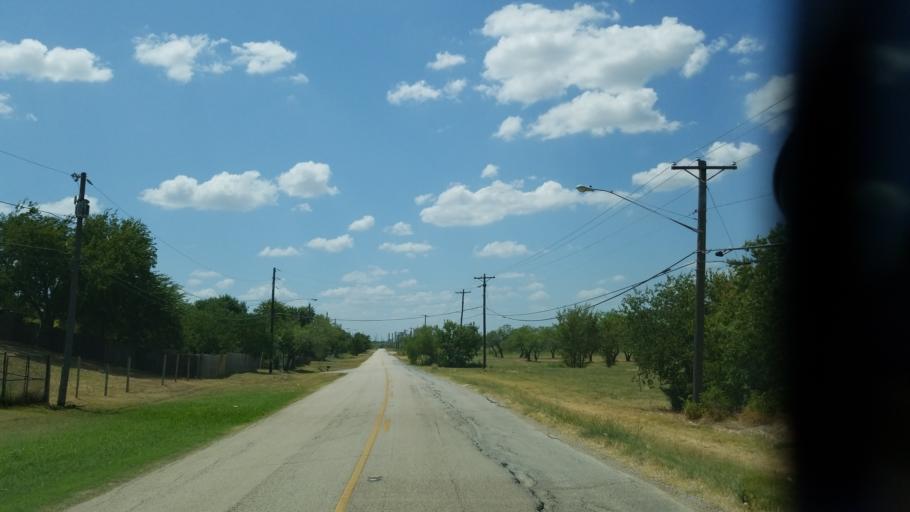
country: US
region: Texas
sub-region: Dallas County
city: Cockrell Hill
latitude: 32.7419
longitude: -96.9276
